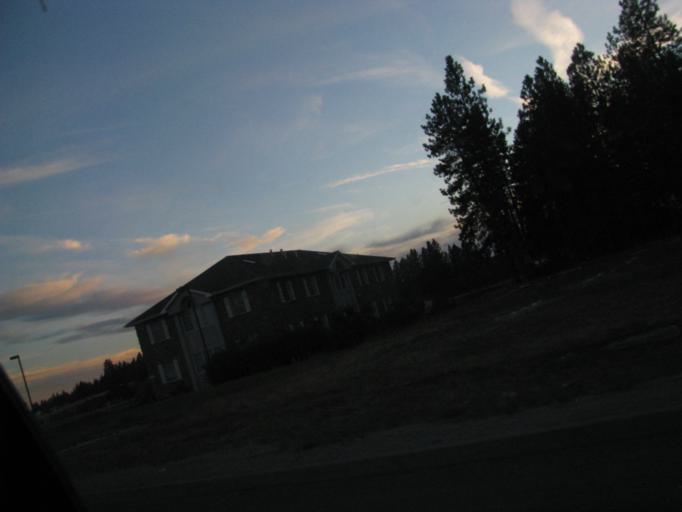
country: US
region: Washington
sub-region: Spokane County
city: Mead
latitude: 47.7905
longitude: -117.3523
